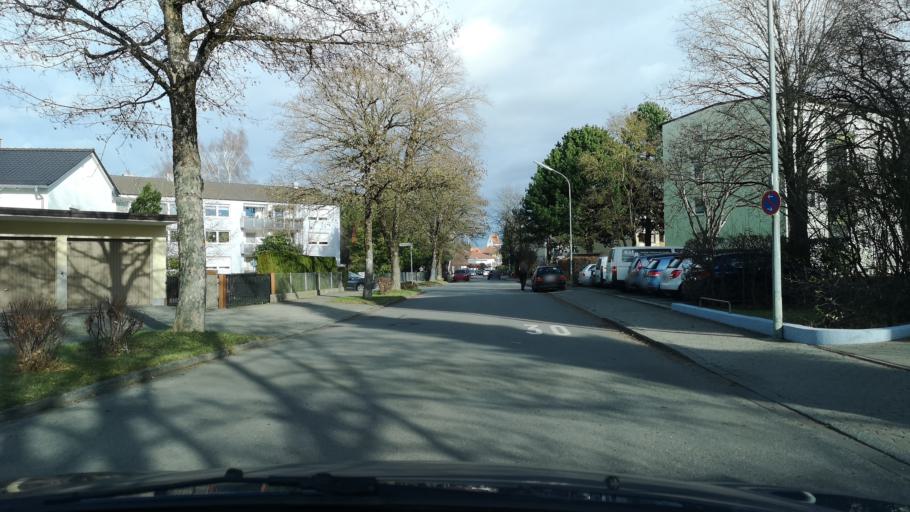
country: DE
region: Bavaria
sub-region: Upper Bavaria
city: Poing
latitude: 48.1672
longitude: 11.8149
